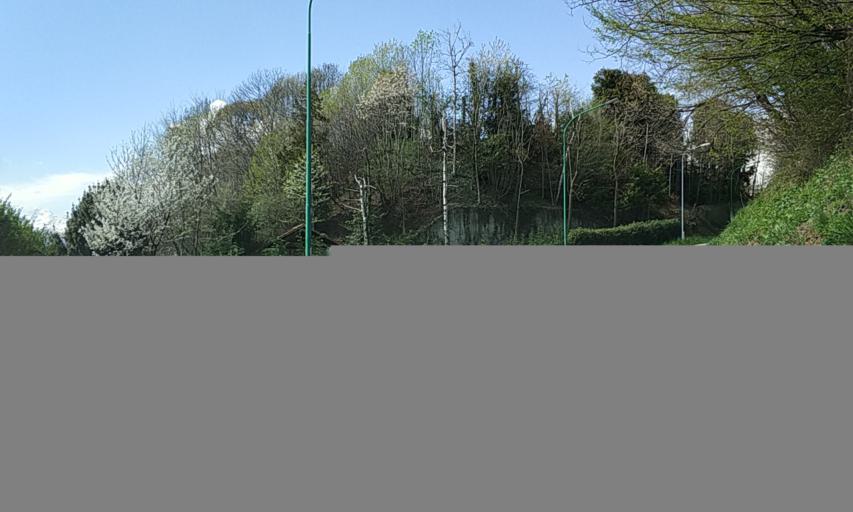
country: IT
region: Piedmont
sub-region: Provincia di Torino
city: San Carlo Canavese
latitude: 45.2476
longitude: 7.5974
